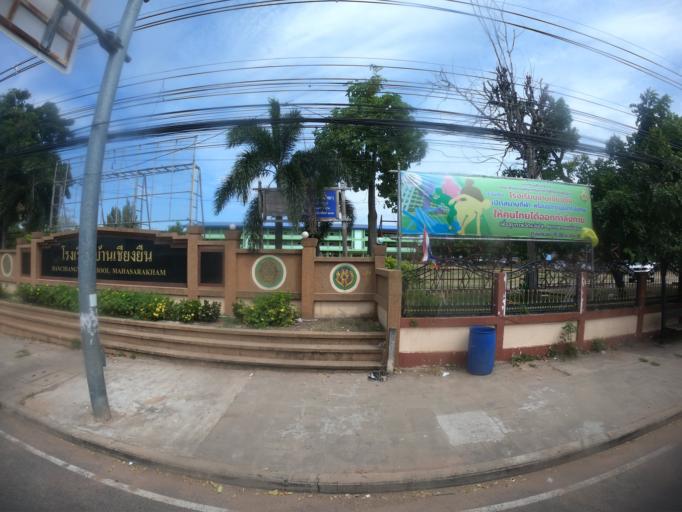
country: TH
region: Maha Sarakham
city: Chiang Yuen
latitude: 16.4112
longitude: 103.0950
